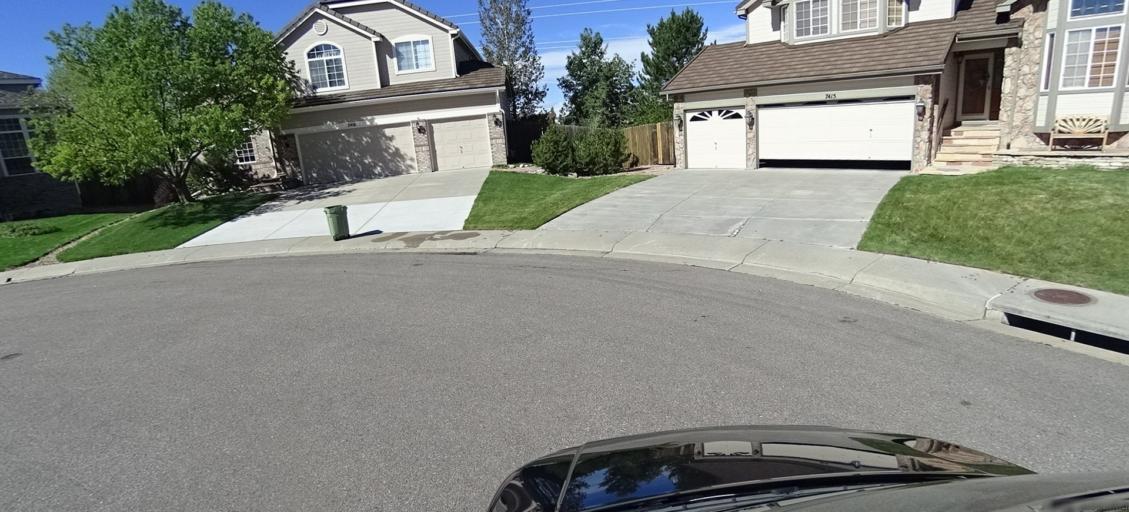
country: US
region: Colorado
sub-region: Douglas County
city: Carriage Club
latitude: 39.5392
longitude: -104.9035
